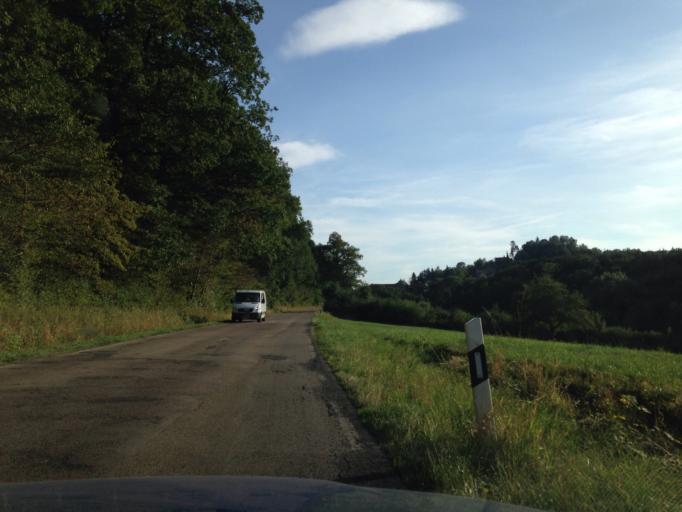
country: DE
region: Bavaria
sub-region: Regierungsbezirk Mittelfranken
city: Thalmassing
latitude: 49.1215
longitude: 11.2133
